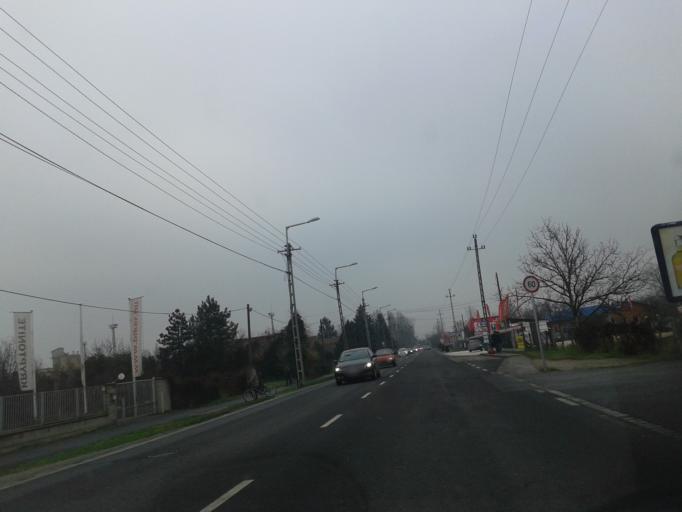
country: HU
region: Budapest
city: Budapest XXII. keruelet
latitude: 47.3949
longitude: 19.0424
